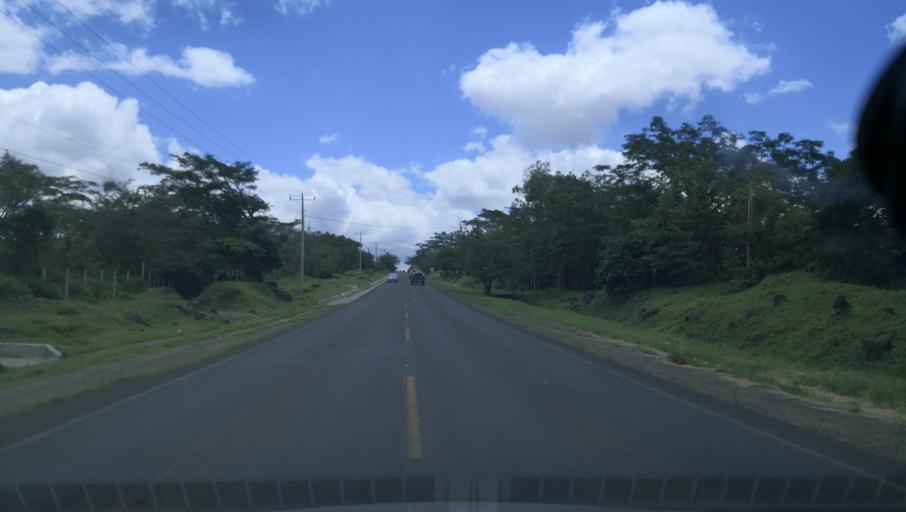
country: NI
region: Esteli
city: Esteli
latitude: 13.1932
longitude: -86.3728
